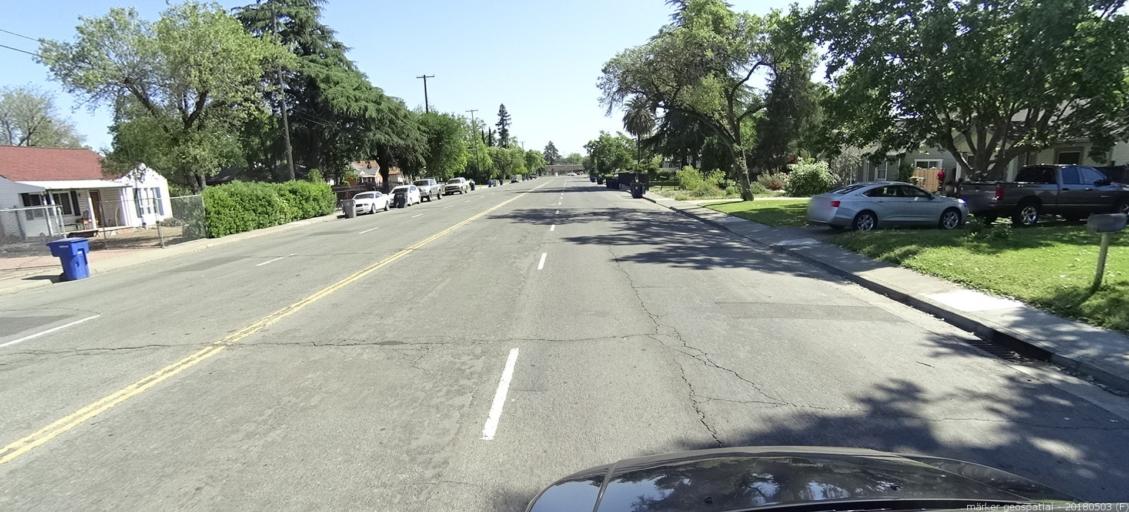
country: US
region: California
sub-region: Sacramento County
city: Arden-Arcade
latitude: 38.6244
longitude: -121.4292
